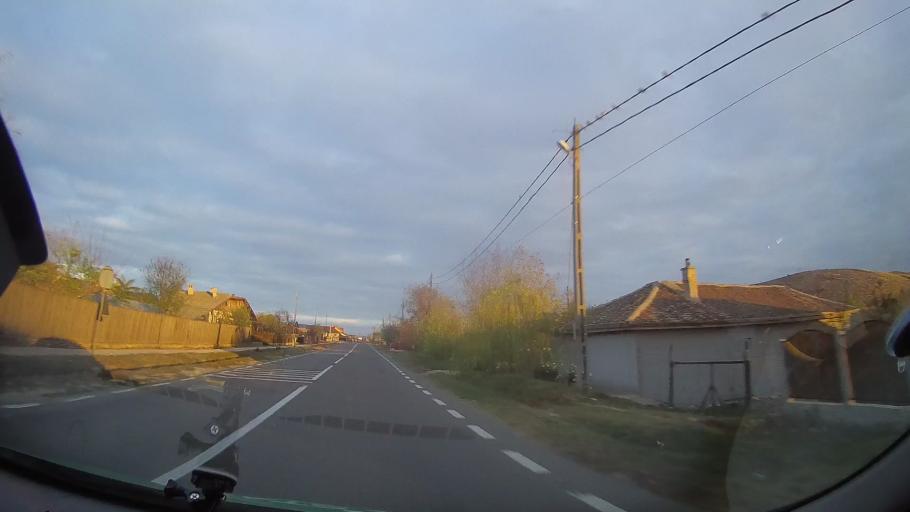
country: RO
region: Tulcea
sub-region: Comuna Nalbant
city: Nicolae Balcescu
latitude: 44.9946
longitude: 28.5845
